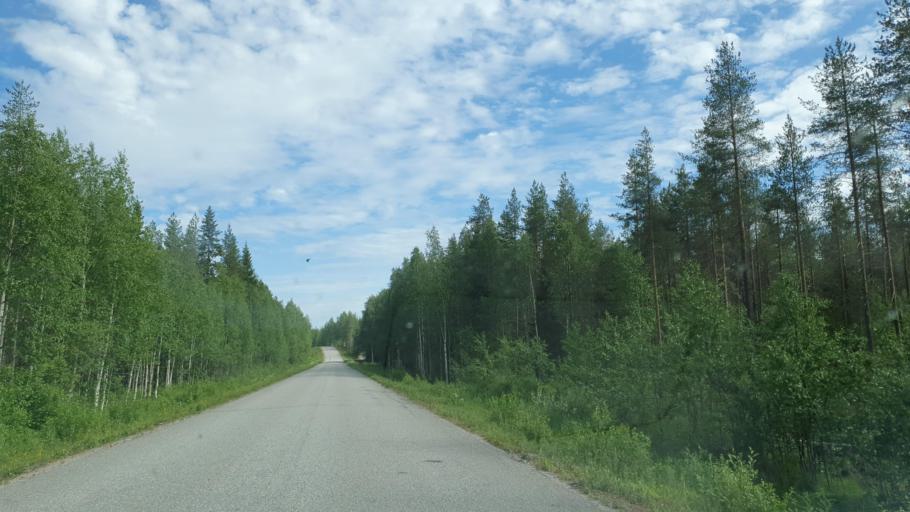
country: FI
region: Kainuu
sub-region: Kehys-Kainuu
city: Suomussalmi
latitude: 64.5459
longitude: 29.2502
